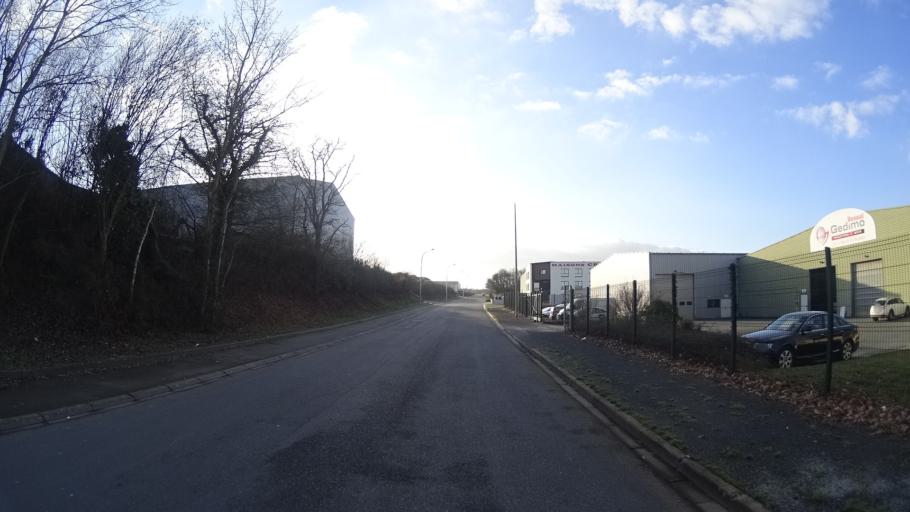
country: FR
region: Pays de la Loire
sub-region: Departement de la Loire-Atlantique
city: Saint-Nicolas-de-Redon
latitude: 47.6315
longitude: -2.0519
